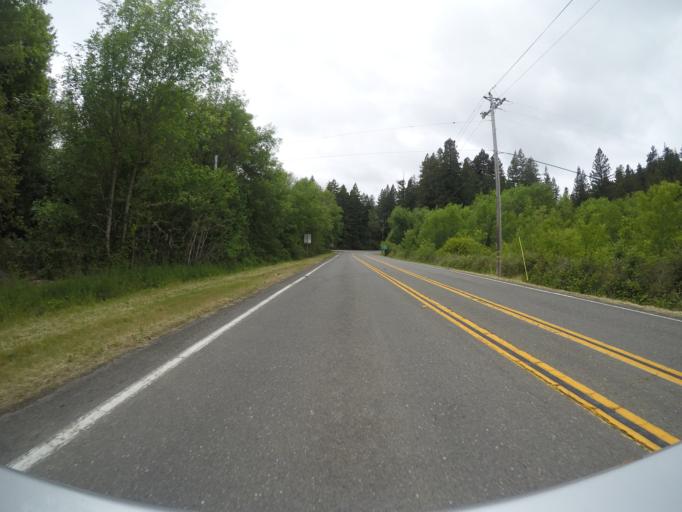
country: US
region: California
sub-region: Humboldt County
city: Rio Dell
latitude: 40.3980
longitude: -123.9454
